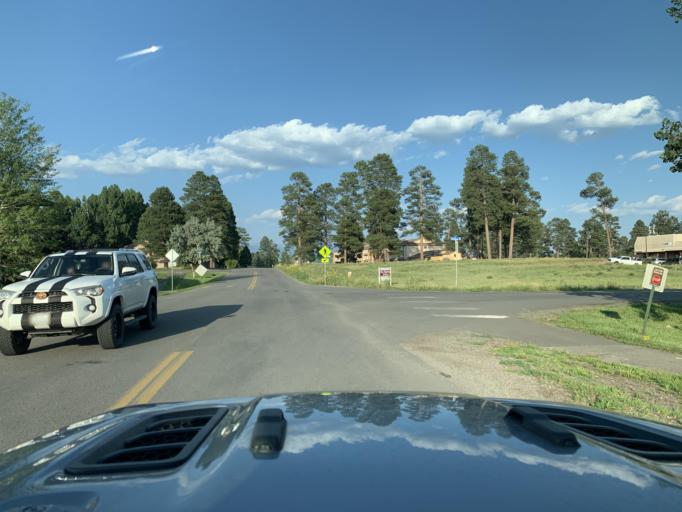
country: US
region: Colorado
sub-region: Archuleta County
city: Pagosa Springs
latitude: 37.2582
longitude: -107.0745
